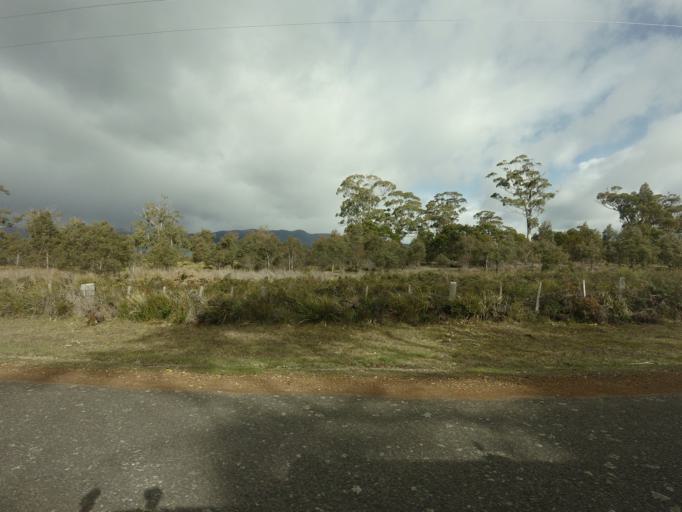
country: AU
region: Tasmania
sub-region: Sorell
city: Sorell
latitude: -42.5413
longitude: 147.9011
